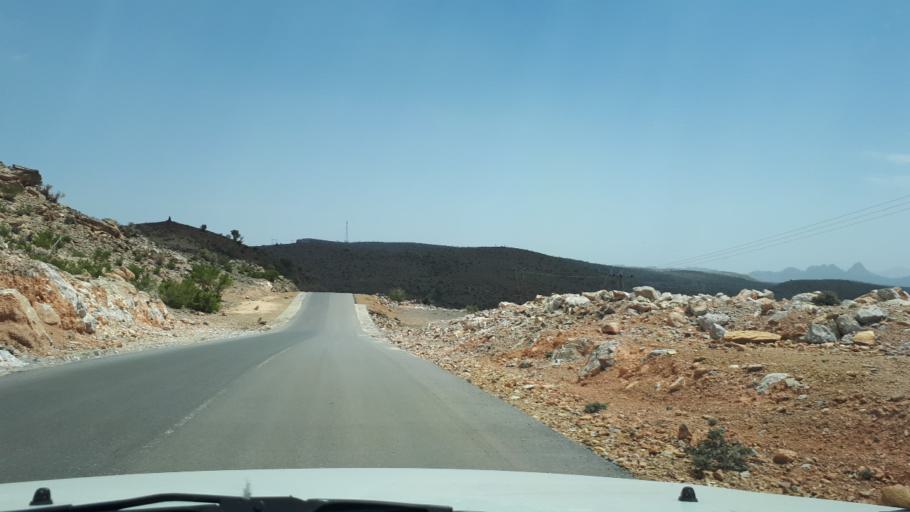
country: OM
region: Al Batinah
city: Rustaq
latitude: 23.2328
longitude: 57.1985
